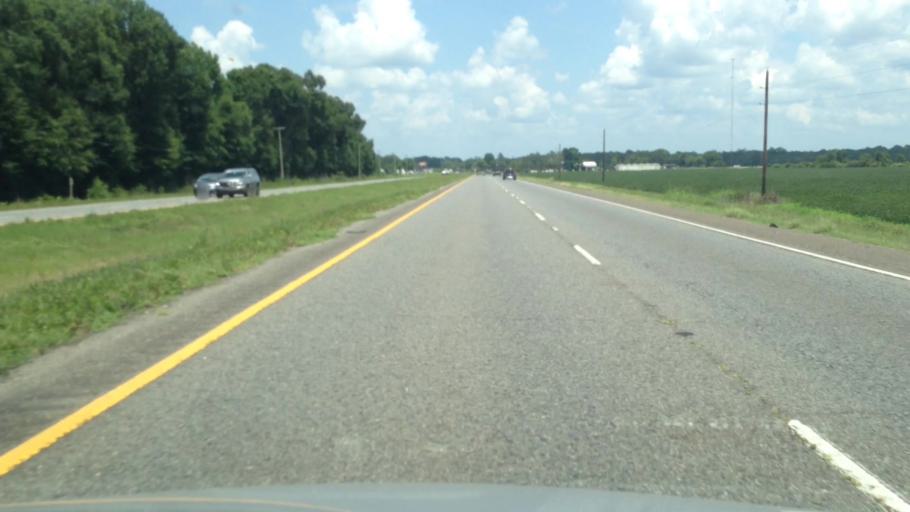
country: US
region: Louisiana
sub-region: Saint Landry Parish
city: Opelousas
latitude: 30.5397
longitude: -92.0381
